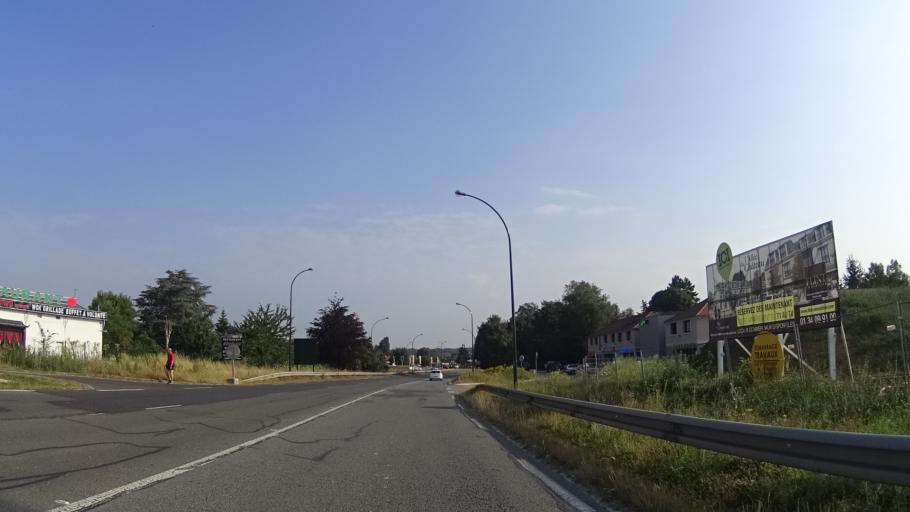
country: FR
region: Ile-de-France
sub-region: Departement du Val-d'Oise
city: Chaumontel
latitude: 49.1207
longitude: 2.4270
